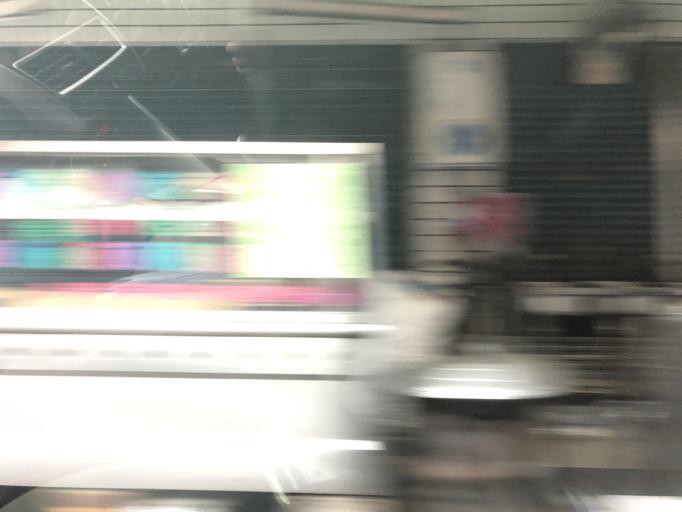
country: TW
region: Taiwan
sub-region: Tainan
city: Tainan
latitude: 23.1293
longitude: 120.2508
